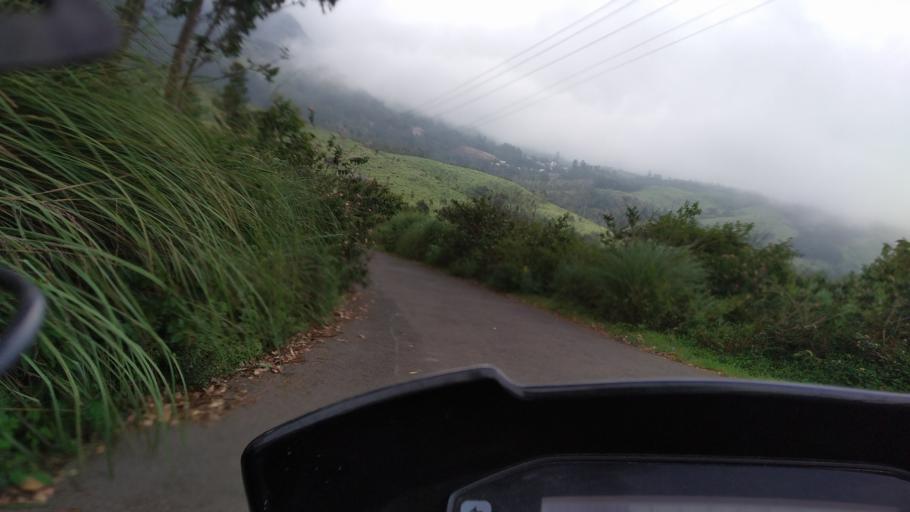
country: IN
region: Kerala
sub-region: Idukki
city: Munnar
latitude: 10.0386
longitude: 77.1821
